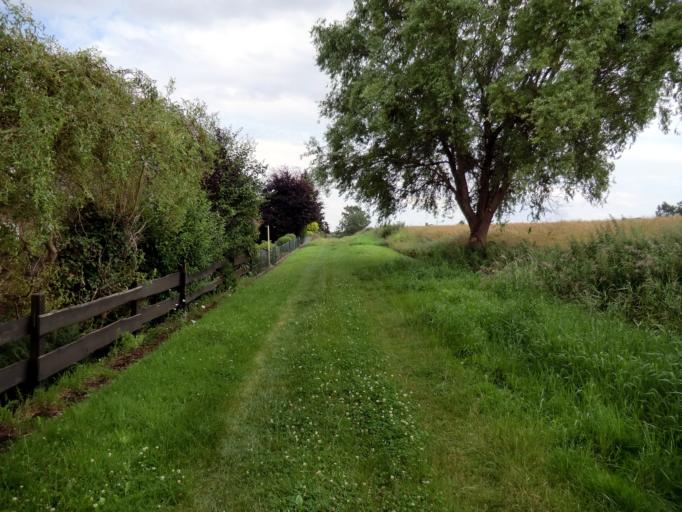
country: DE
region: North Rhine-Westphalia
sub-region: Regierungsbezirk Detmold
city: Hiddenhausen
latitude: 52.1661
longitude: 8.6077
